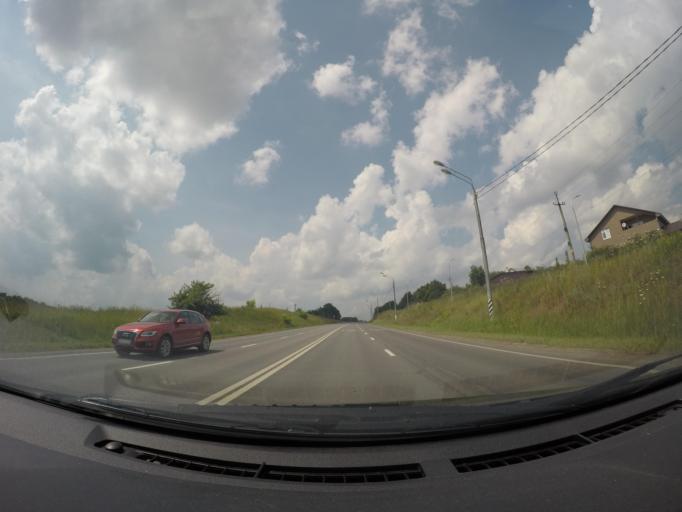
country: RU
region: Moskovskaya
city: Bronnitsy
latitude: 55.4720
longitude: 38.1934
